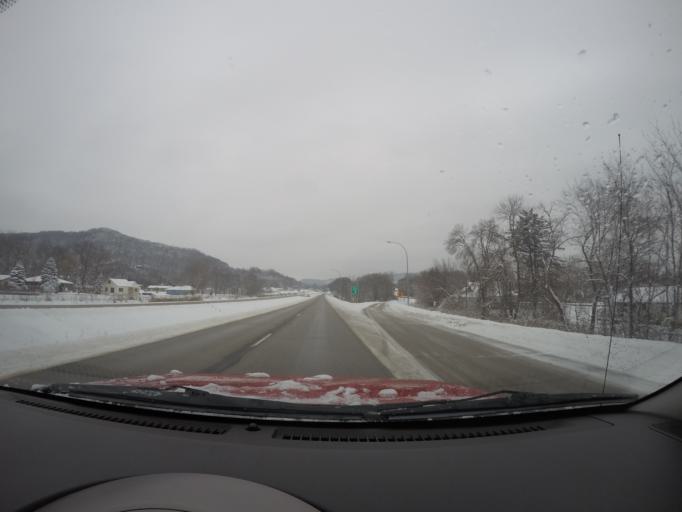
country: US
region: Wisconsin
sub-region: La Crosse County
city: Brice Prairie
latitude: 43.9071
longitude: -91.3534
